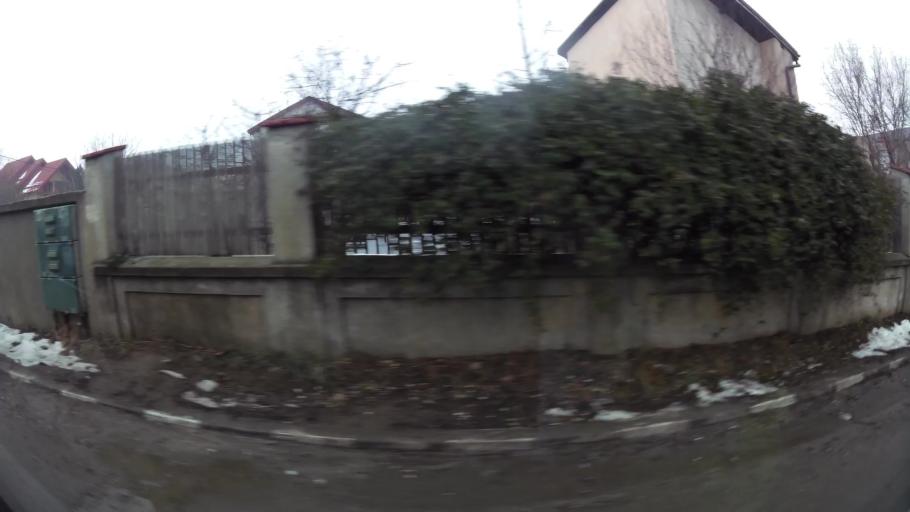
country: RO
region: Ilfov
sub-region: Comuna Chiajna
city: Rosu
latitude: 44.4481
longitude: 26.0064
